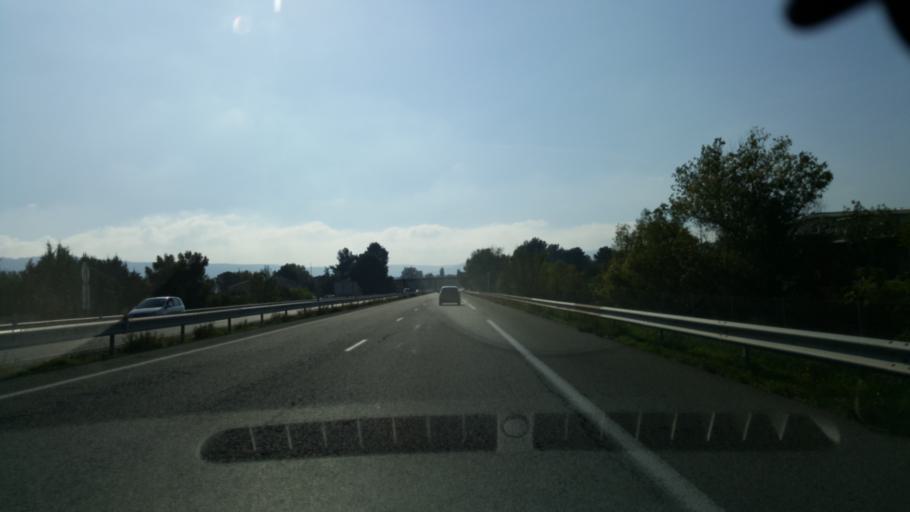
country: FR
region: Provence-Alpes-Cote d'Azur
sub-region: Departement des Bouches-du-Rhone
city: Aubagne
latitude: 43.3133
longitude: 5.5839
